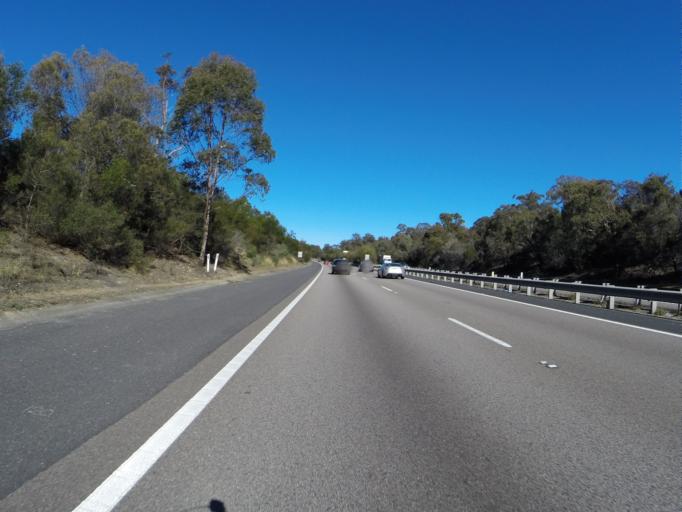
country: AU
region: New South Wales
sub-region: Wollondilly
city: Douglas Park
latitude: -34.2394
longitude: 150.6611
